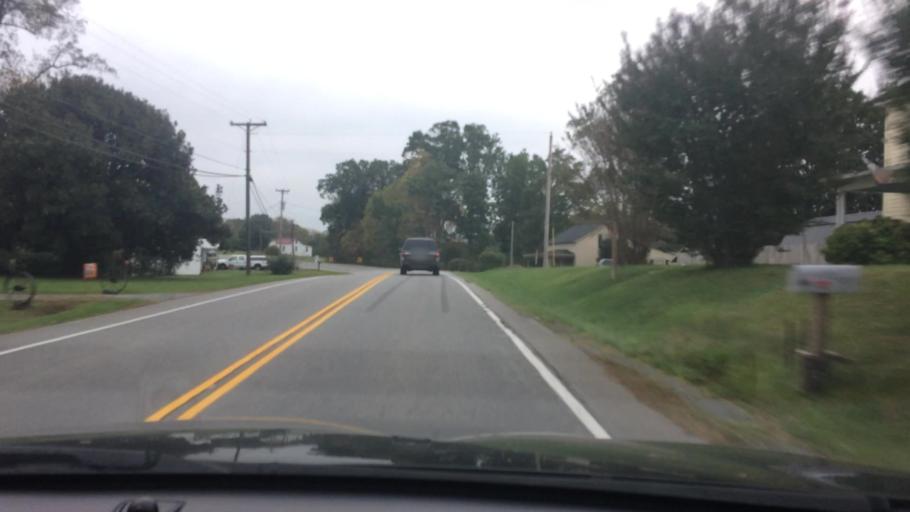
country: US
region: Virginia
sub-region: Franklin County
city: Henry Fork
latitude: 37.0160
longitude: -79.8293
